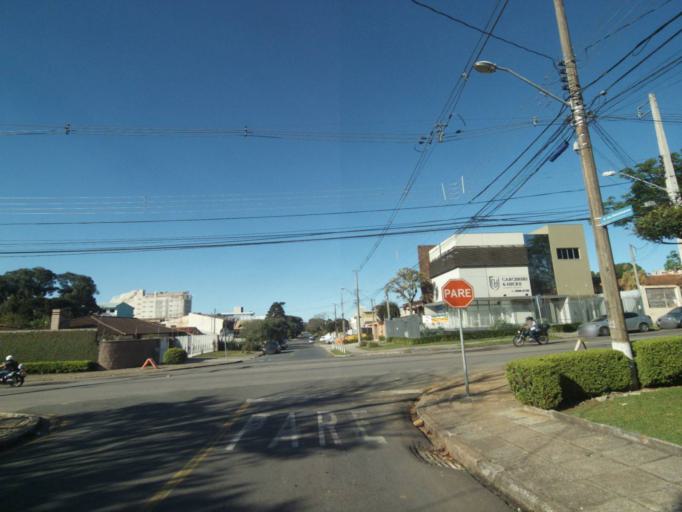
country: BR
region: Parana
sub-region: Curitiba
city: Curitiba
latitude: -25.3953
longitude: -49.2514
